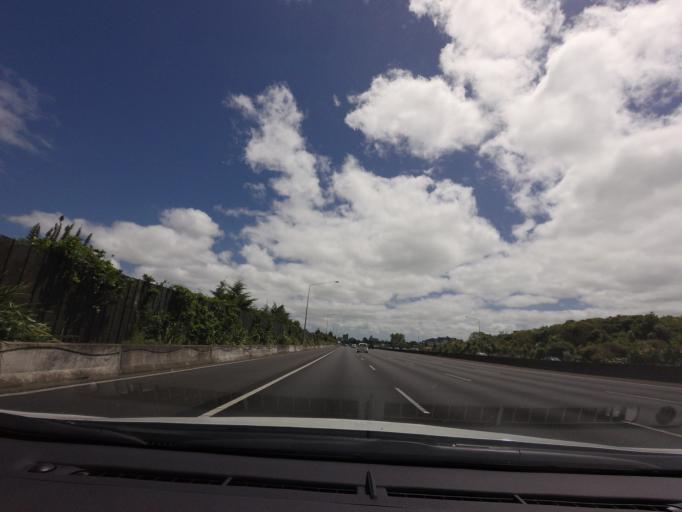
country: NZ
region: Auckland
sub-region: Auckland
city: Auckland
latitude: -36.8686
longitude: 174.7377
